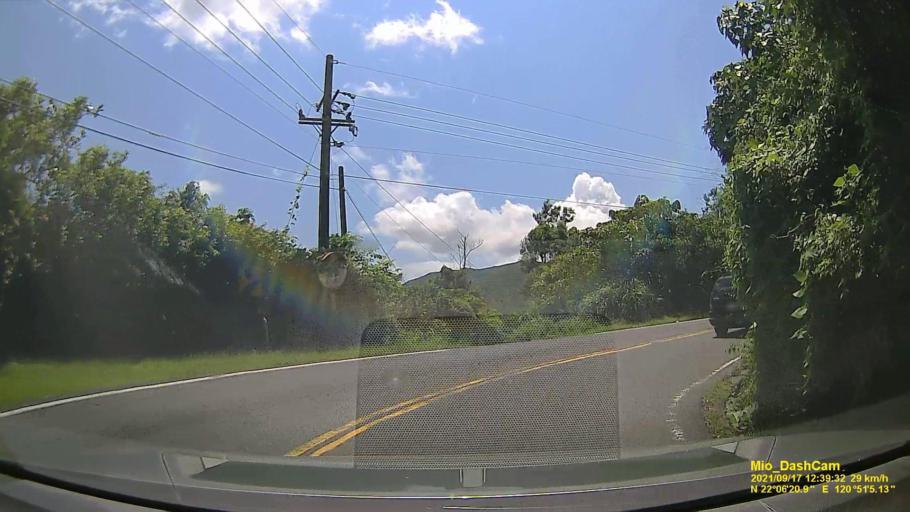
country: TW
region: Taiwan
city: Hengchun
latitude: 22.1058
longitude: 120.8514
